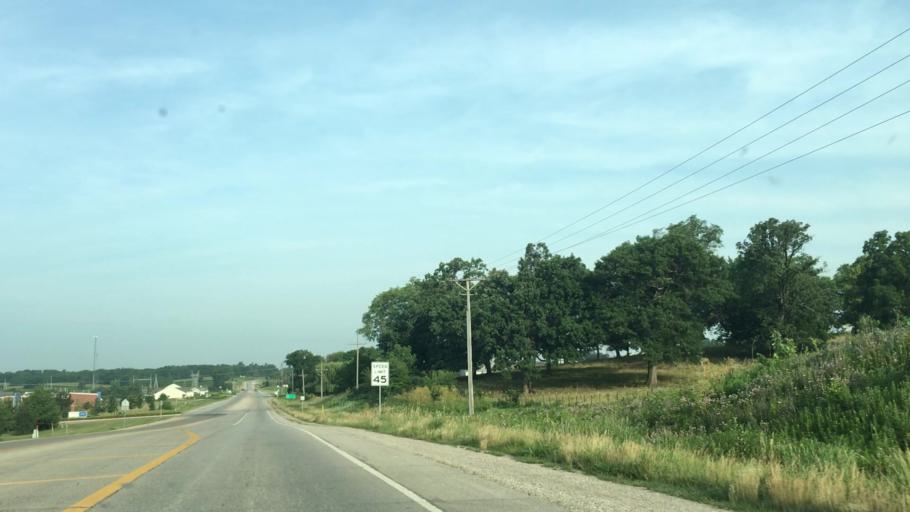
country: US
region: Iowa
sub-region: Johnson County
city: Tiffin
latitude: 41.7076
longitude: -91.6695
